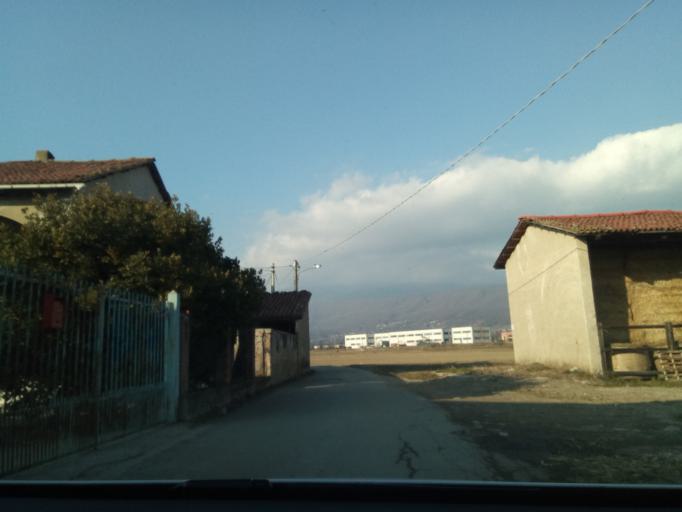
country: IT
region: Piedmont
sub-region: Provincia di Torino
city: Burolo
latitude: 45.4640
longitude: 7.9208
